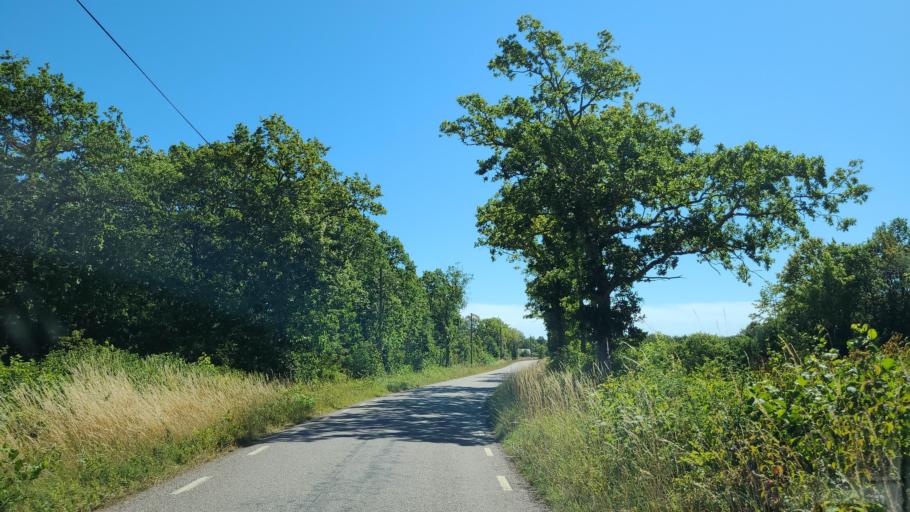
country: SE
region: Kalmar
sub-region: Borgholms Kommun
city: Borgholm
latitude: 56.7612
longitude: 16.6558
